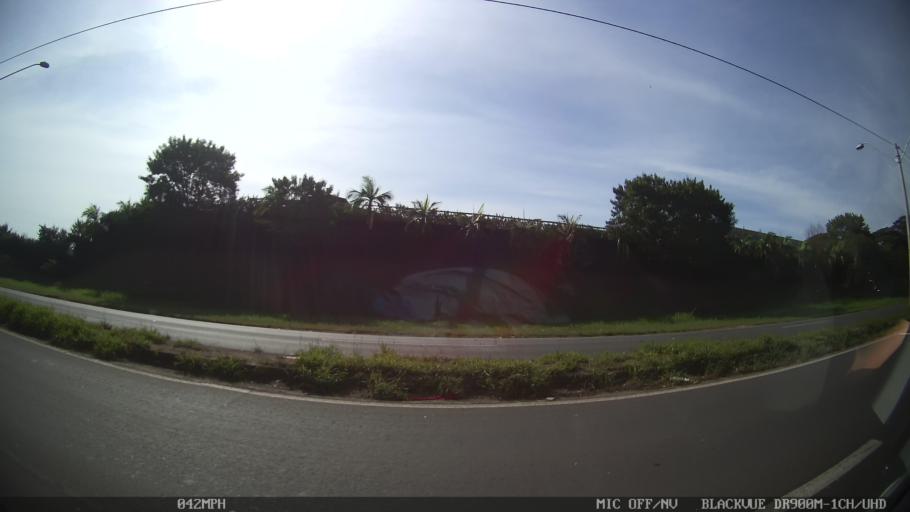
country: BR
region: Sao Paulo
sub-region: Piracicaba
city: Piracicaba
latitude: -22.6908
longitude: -47.6662
